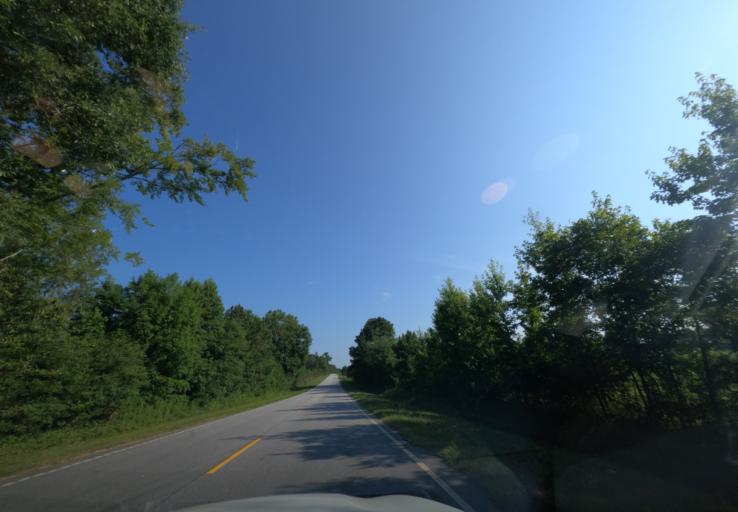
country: US
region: South Carolina
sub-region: Edgefield County
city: Edgefield
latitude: 33.9526
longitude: -82.0470
